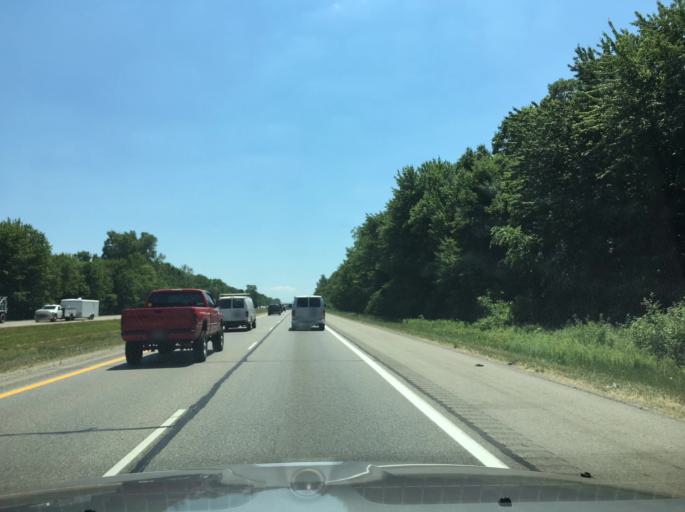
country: US
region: Michigan
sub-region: Macomb County
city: Shelby
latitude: 42.6528
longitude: -83.0143
